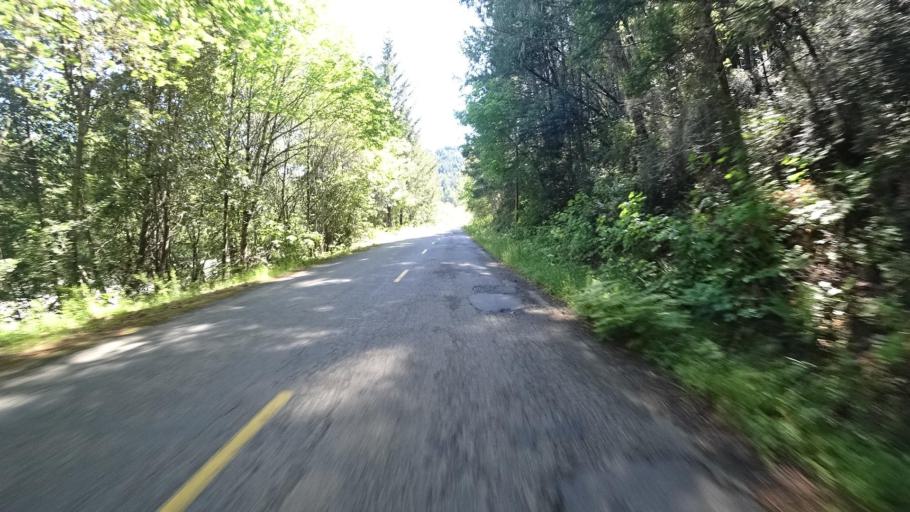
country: US
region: California
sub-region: Humboldt County
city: Rio Dell
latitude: 40.2297
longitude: -124.1472
